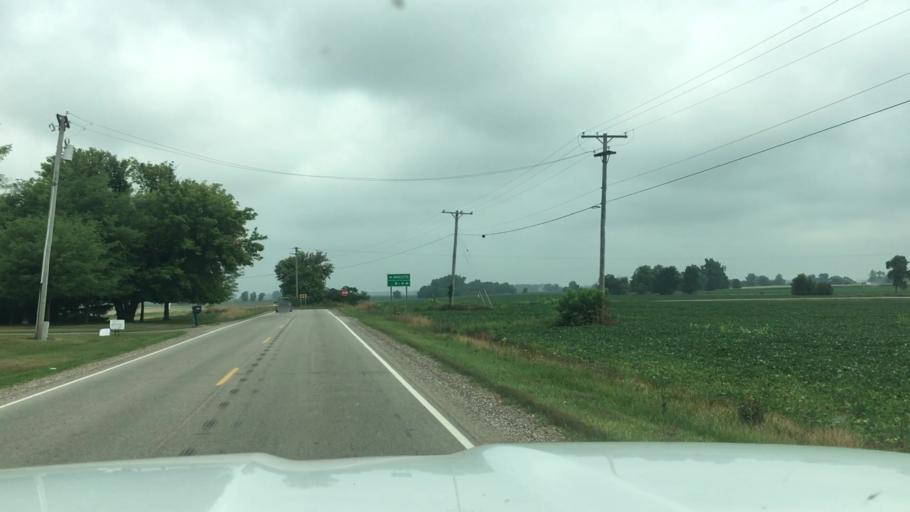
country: US
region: Michigan
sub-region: Sanilac County
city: Marlette
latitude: 43.3286
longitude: -82.9843
